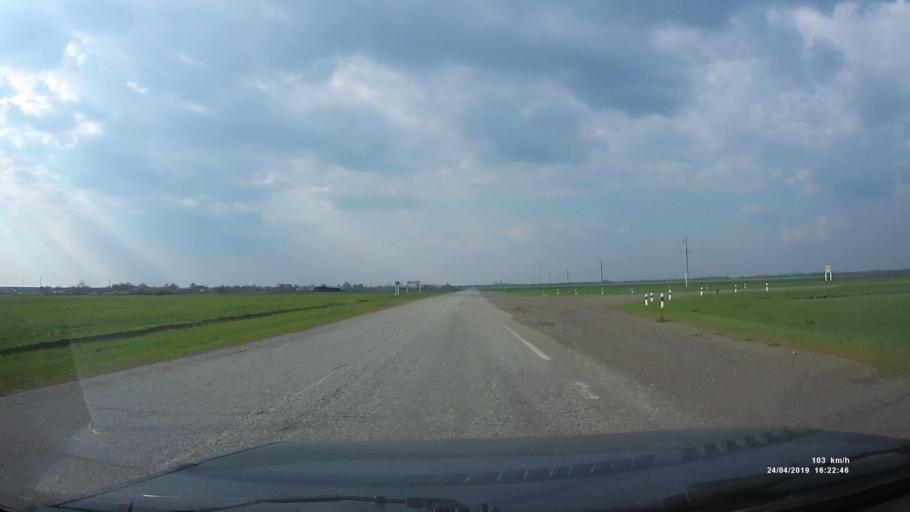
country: RU
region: Rostov
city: Orlovskiy
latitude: 46.8245
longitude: 42.0534
